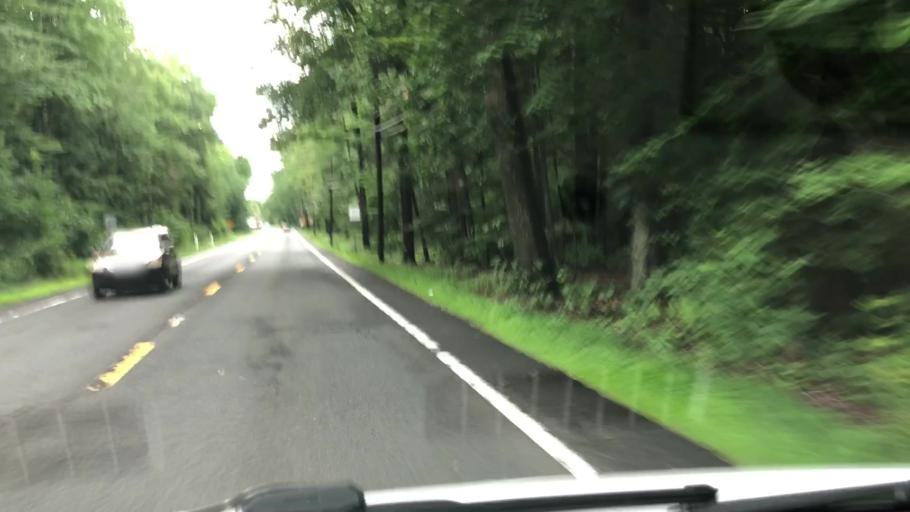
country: US
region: Massachusetts
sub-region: Franklin County
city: Whately
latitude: 42.4549
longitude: -72.6247
